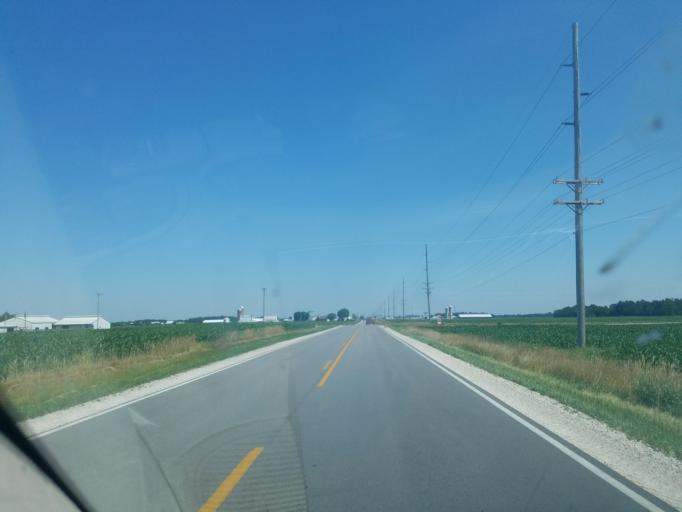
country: US
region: Ohio
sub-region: Mercer County
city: Saint Henry
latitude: 40.4494
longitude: -84.6481
